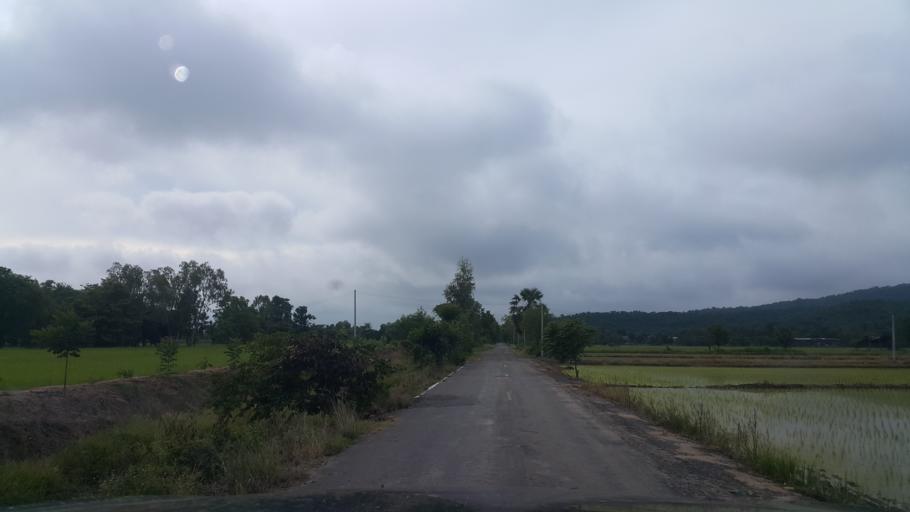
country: TH
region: Sukhothai
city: Sawankhalok
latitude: 17.3092
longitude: 99.7011
